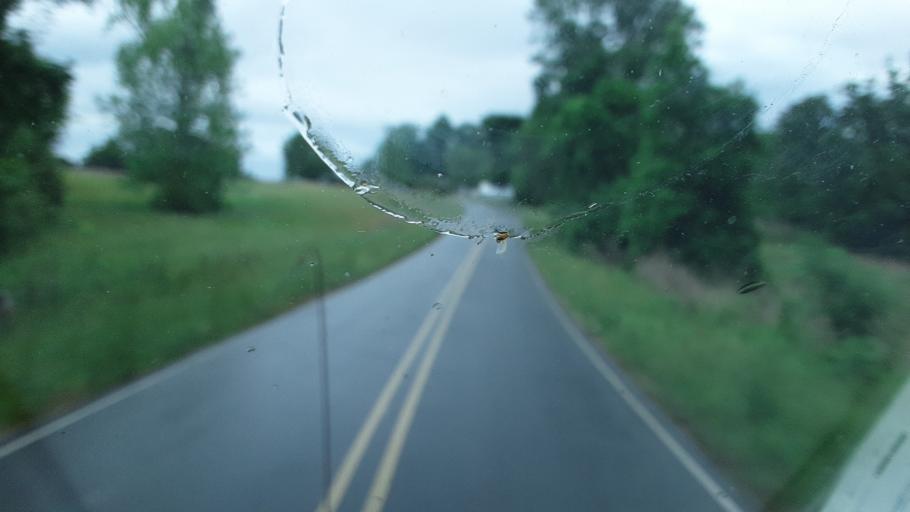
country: US
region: North Carolina
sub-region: Yadkin County
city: Jonesville
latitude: 36.0765
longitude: -80.8295
